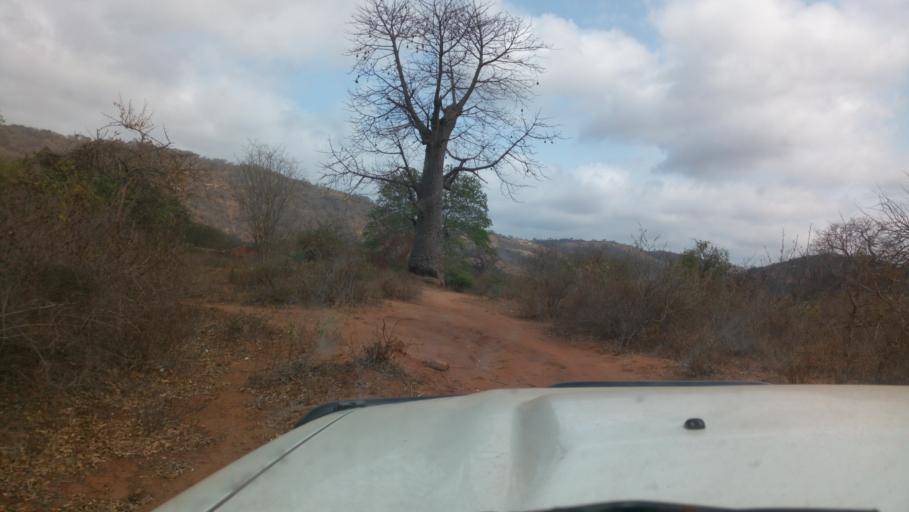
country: KE
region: Kitui
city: Kitui
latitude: -1.8397
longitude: 38.2984
